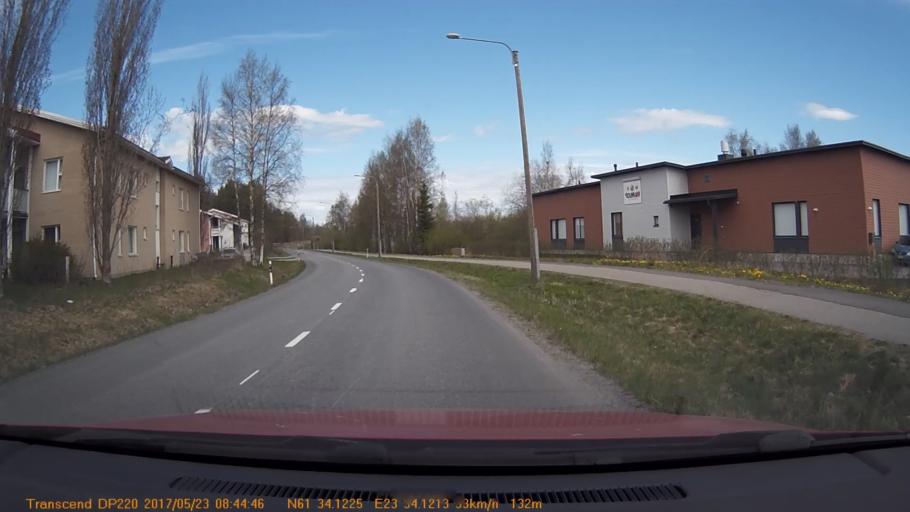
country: FI
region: Pirkanmaa
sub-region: Tampere
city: Yloejaervi
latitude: 61.5687
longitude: 23.5689
